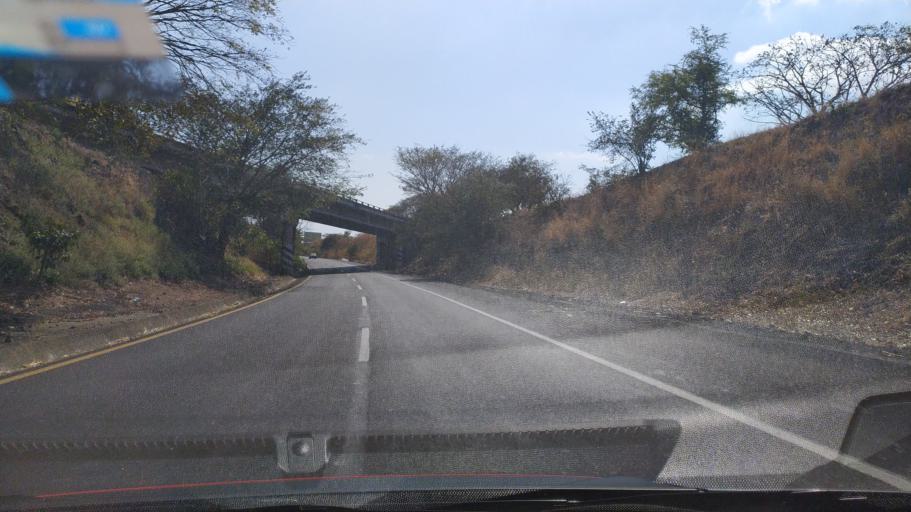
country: MX
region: Colima
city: Colima
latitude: 19.2648
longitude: -103.6815
